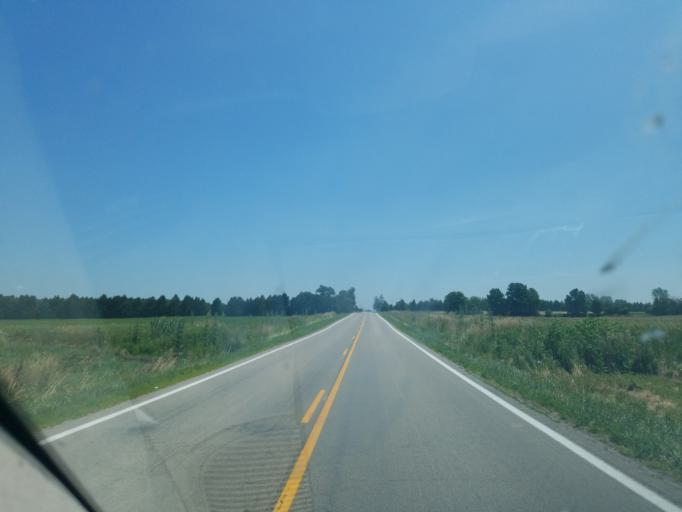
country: US
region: Ohio
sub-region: Mercer County
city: Rockford
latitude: 40.7424
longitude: -84.7243
